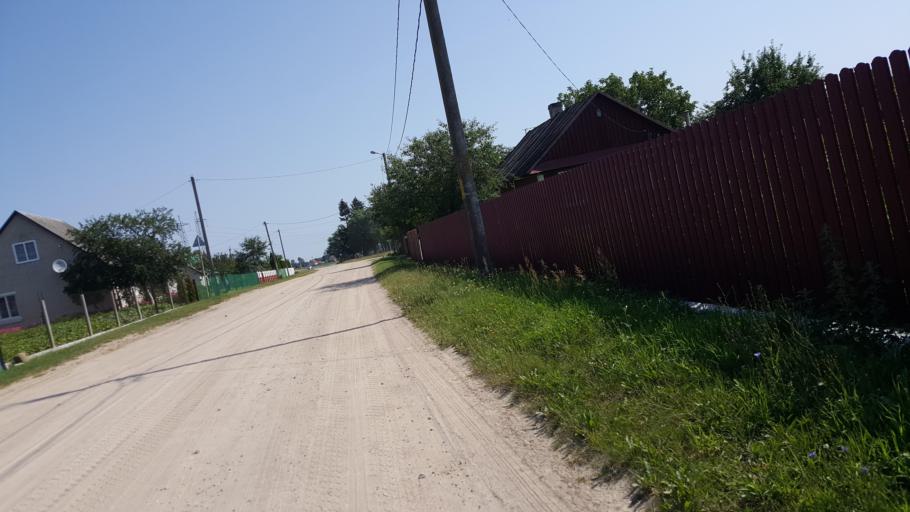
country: BY
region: Brest
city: Zhabinka
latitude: 52.2096
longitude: 23.9978
